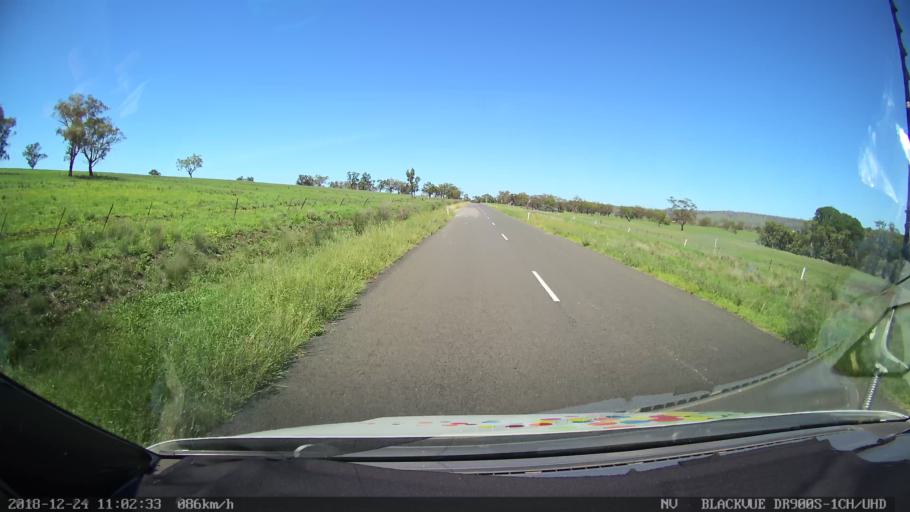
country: AU
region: New South Wales
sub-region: Upper Hunter Shire
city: Merriwa
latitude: -32.0864
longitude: 150.3741
